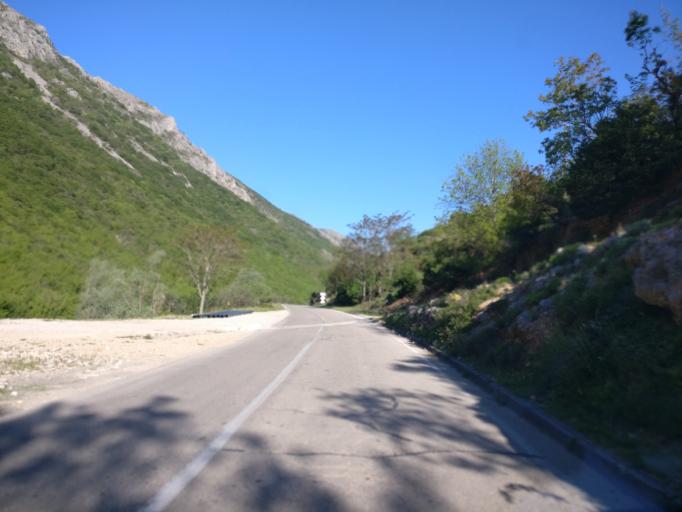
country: BA
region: Federation of Bosnia and Herzegovina
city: Stolac
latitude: 43.0793
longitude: 18.0158
